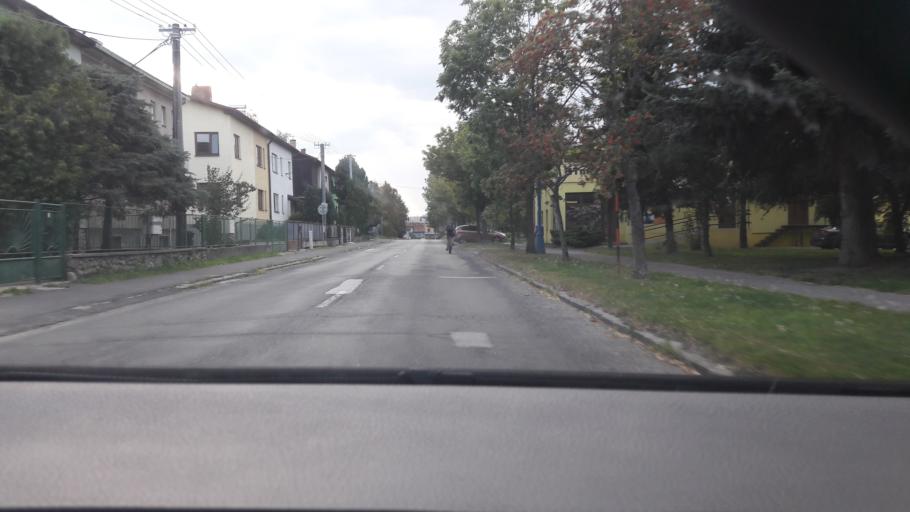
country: SK
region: Presovsky
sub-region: Okres Poprad
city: Poprad
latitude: 49.0653
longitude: 20.2806
